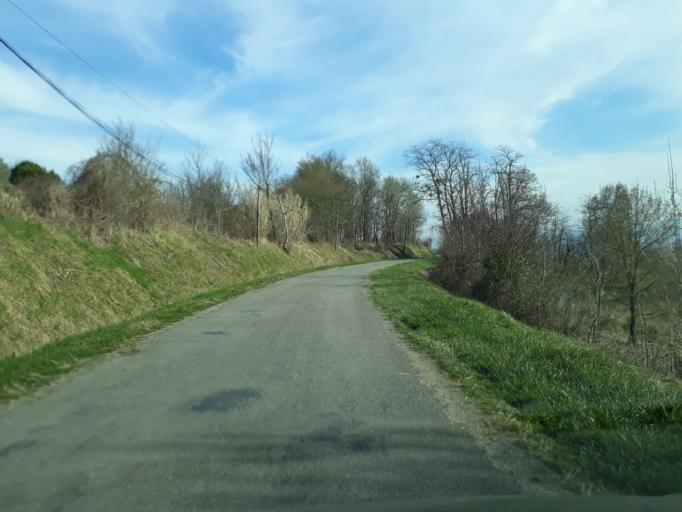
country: FR
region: Midi-Pyrenees
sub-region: Departement de la Haute-Garonne
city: Montesquieu-Volvestre
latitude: 43.1812
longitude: 1.3135
